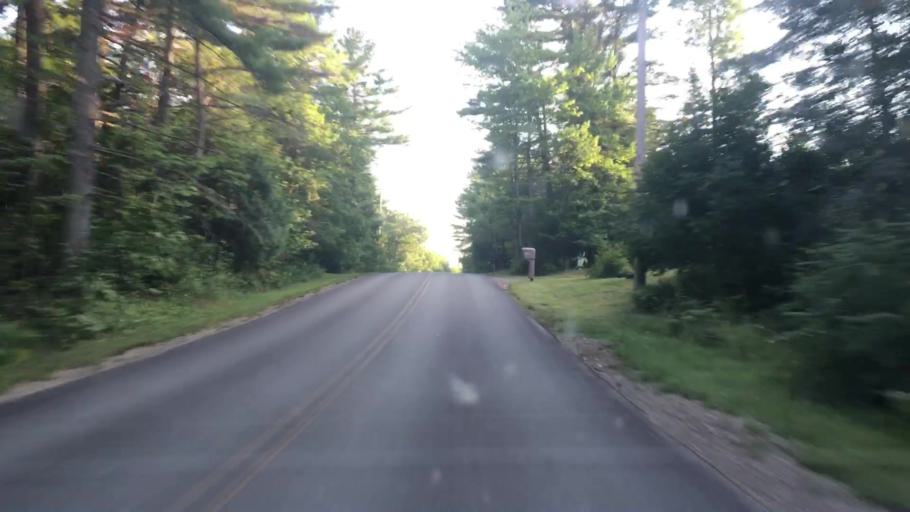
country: US
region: Maine
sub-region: Penobscot County
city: Hampden
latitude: 44.7005
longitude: -68.8938
